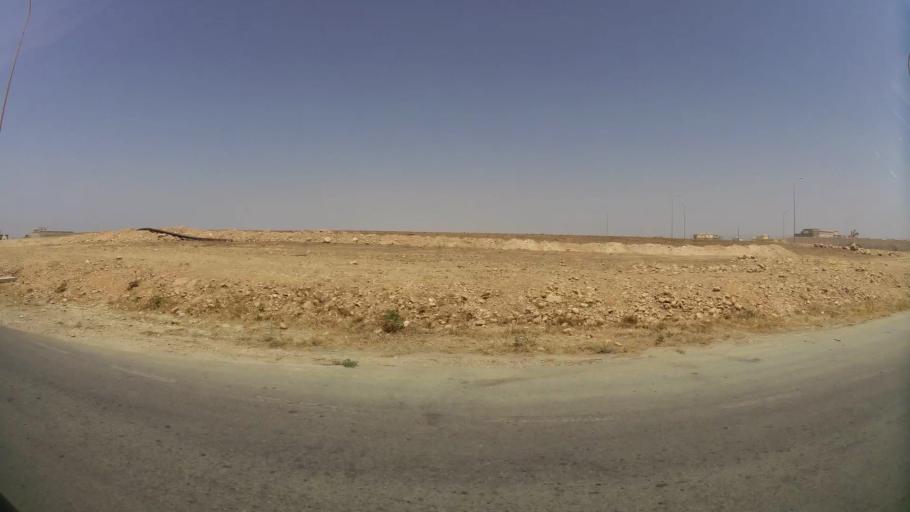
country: OM
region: Zufar
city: Salalah
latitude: 17.0833
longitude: 54.1888
